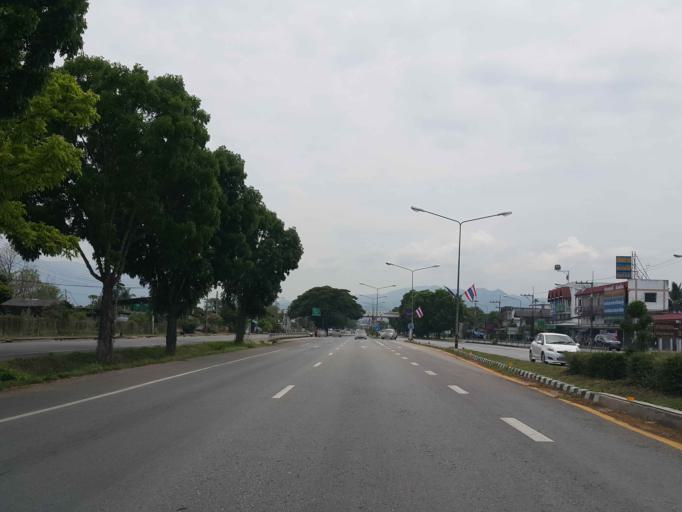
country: TH
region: Lampang
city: Sop Prap
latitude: 17.8874
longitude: 99.3390
